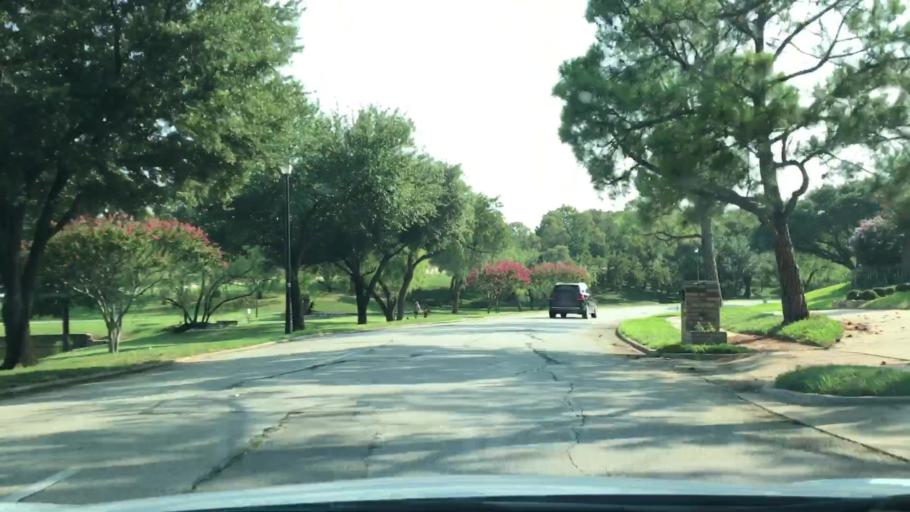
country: US
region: Texas
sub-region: Dallas County
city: Irving
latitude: 32.8453
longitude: -96.9373
